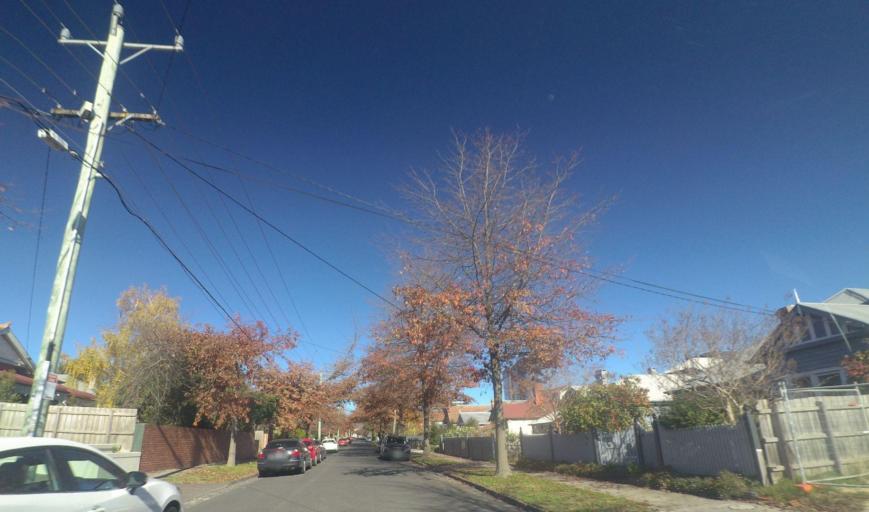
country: AU
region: Victoria
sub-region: Whitehorse
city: Box Hill
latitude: -37.8146
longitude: 145.1271
